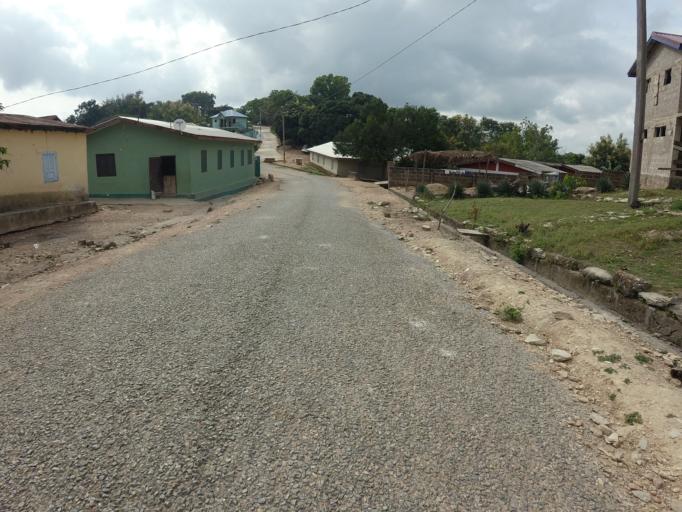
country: TG
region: Plateaux
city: Kpalime
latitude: 6.8895
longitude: 0.4543
